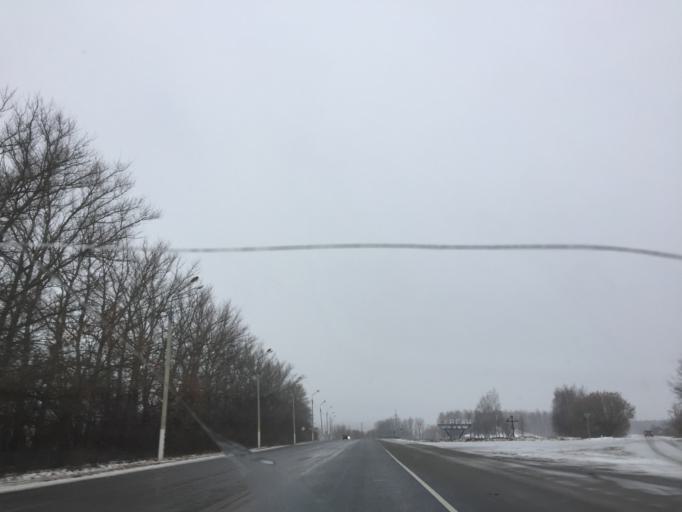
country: RU
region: Tula
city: Plavsk
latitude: 53.7265
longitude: 37.3026
